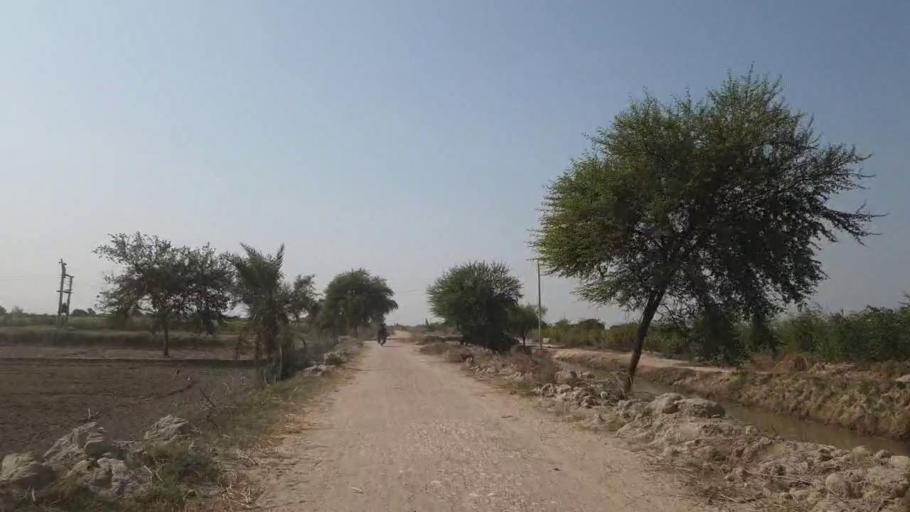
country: PK
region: Sindh
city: Bulri
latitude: 24.9510
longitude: 68.3676
